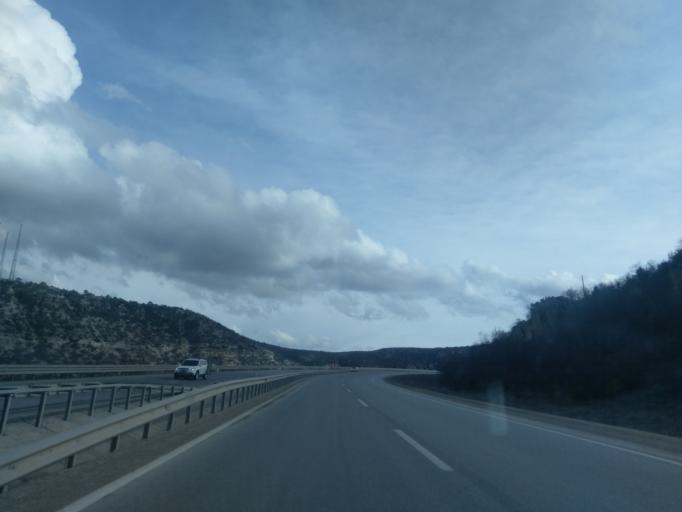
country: TR
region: Kuetahya
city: Sabuncu
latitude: 39.5634
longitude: 30.0744
